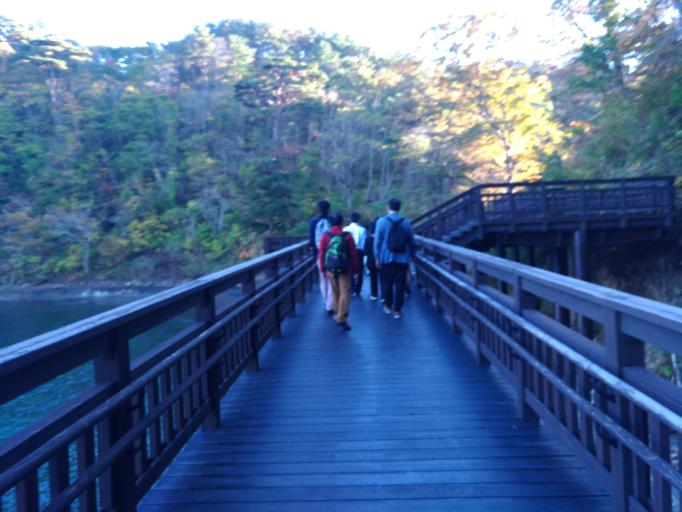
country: JP
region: Iwate
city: Miyako
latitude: 39.6475
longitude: 141.9794
